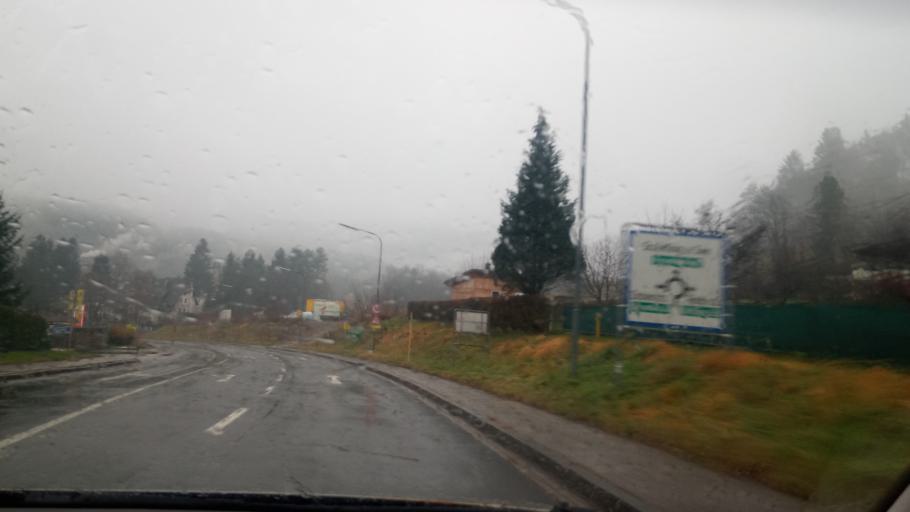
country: AT
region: Carinthia
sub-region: Politischer Bezirk Klagenfurt Land
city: Keutschach am See
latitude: 46.5914
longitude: 14.1719
